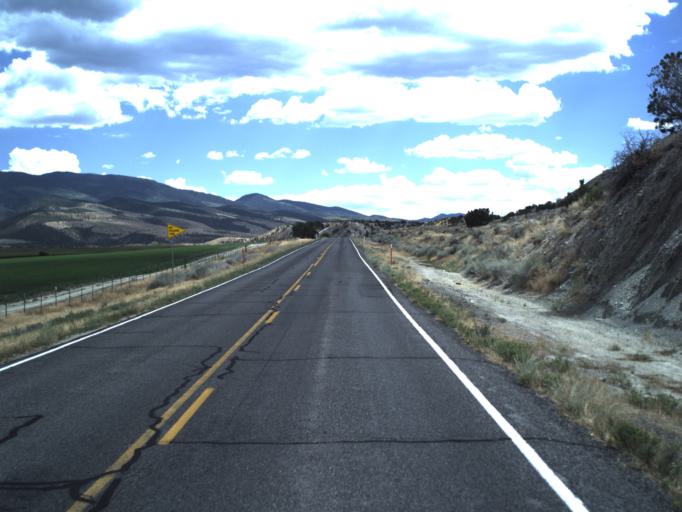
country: US
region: Utah
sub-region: Sanpete County
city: Gunnison
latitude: 39.1393
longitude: -111.7316
